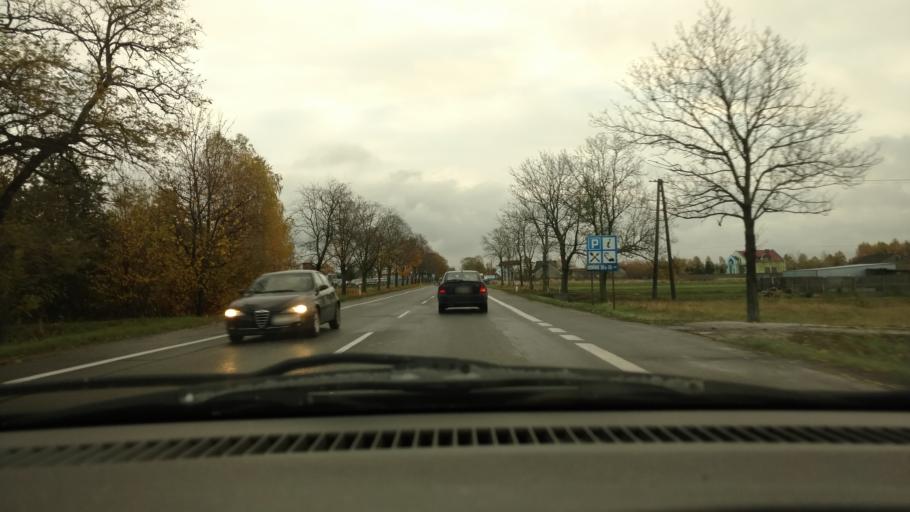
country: PL
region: Lodz Voivodeship
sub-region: Powiat zdunskowolski
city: Zdunska Wola
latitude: 51.5915
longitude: 19.0204
